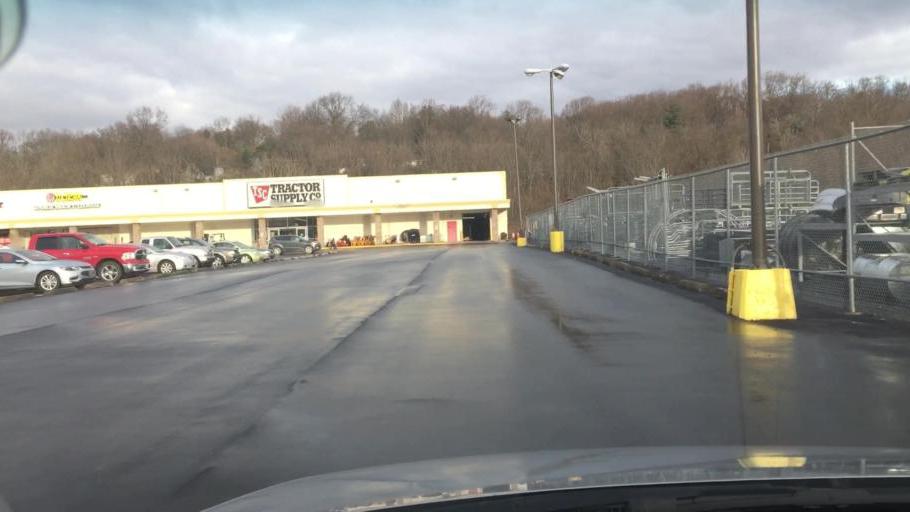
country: US
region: Pennsylvania
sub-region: Columbia County
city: Espy
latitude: 41.0073
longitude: -76.4307
